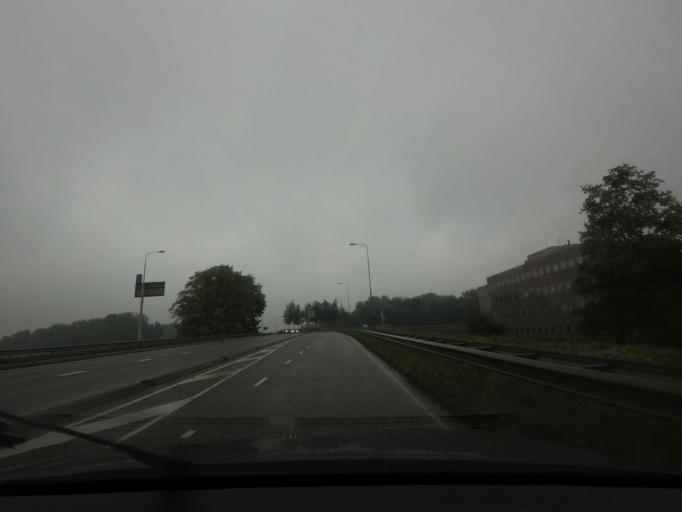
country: NL
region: North Holland
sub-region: Gemeente Aalsmeer
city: Aalsmeer
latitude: 52.3416
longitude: 4.7638
